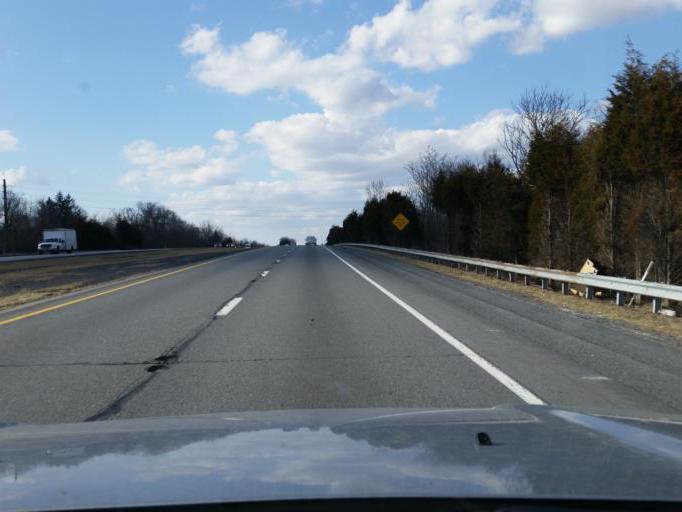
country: US
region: Pennsylvania
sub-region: Dauphin County
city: Middletown
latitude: 40.2065
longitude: -76.7053
